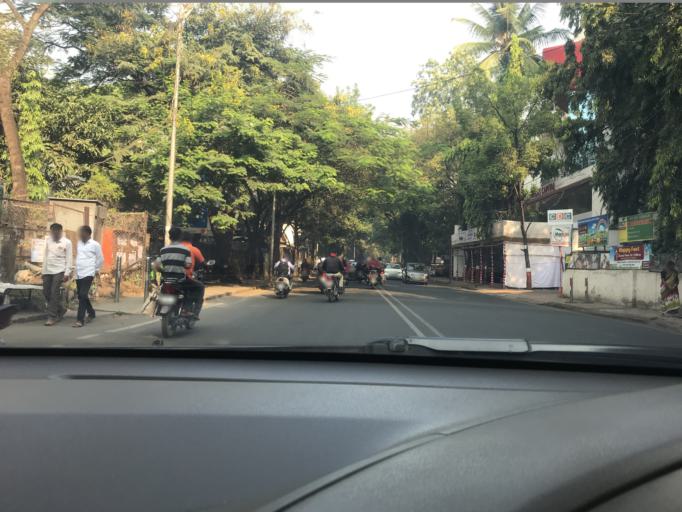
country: IN
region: Maharashtra
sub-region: Pune Division
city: Pune
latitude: 18.5109
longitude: 73.8294
